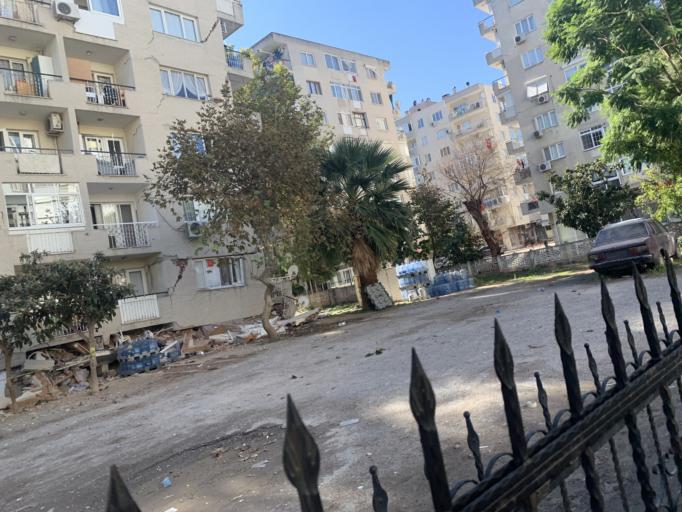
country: TR
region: Izmir
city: Bornova
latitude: 38.4635
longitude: 27.1895
